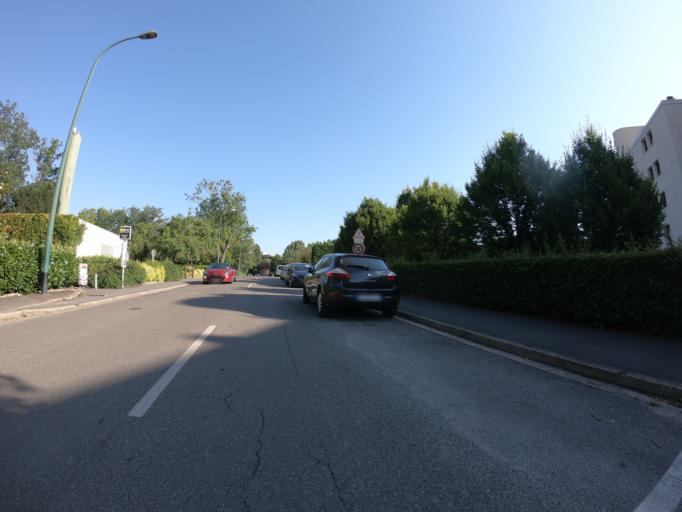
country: FR
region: Ile-de-France
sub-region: Departement de l'Essonne
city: Verrieres-le-Buisson
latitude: 48.7483
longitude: 2.2742
